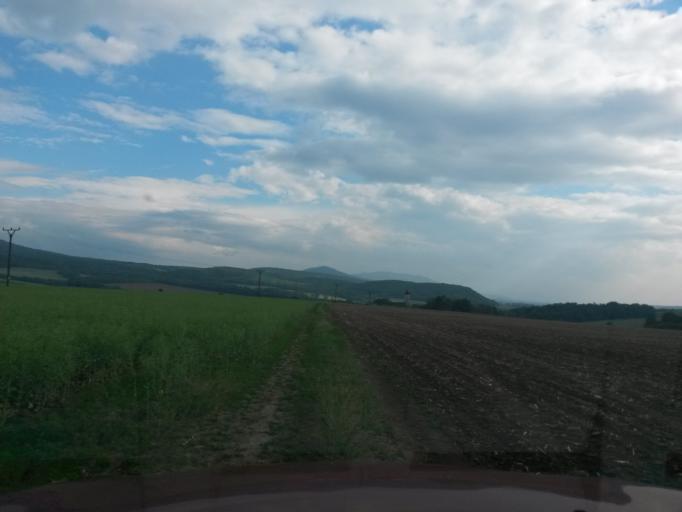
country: SK
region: Kosicky
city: Secovce
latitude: 48.7435
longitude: 21.4612
